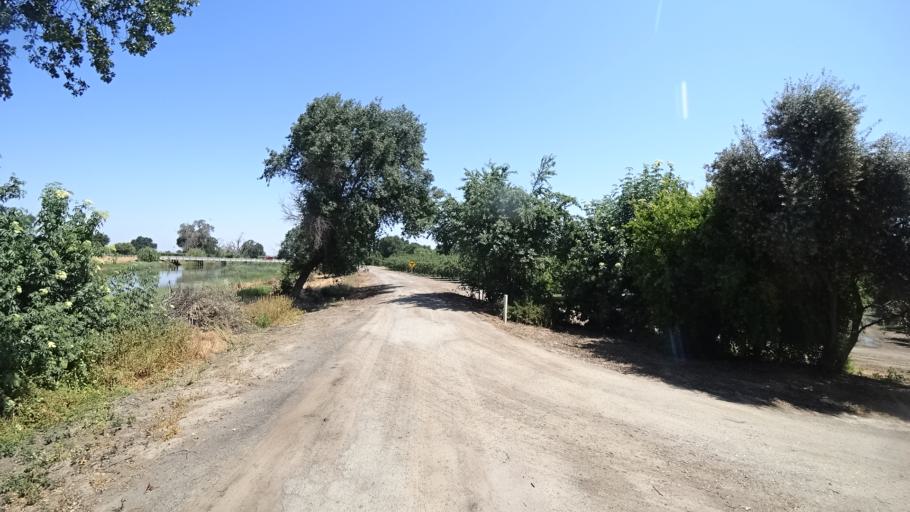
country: US
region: California
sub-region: Kings County
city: Lemoore
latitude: 36.3664
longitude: -119.8028
